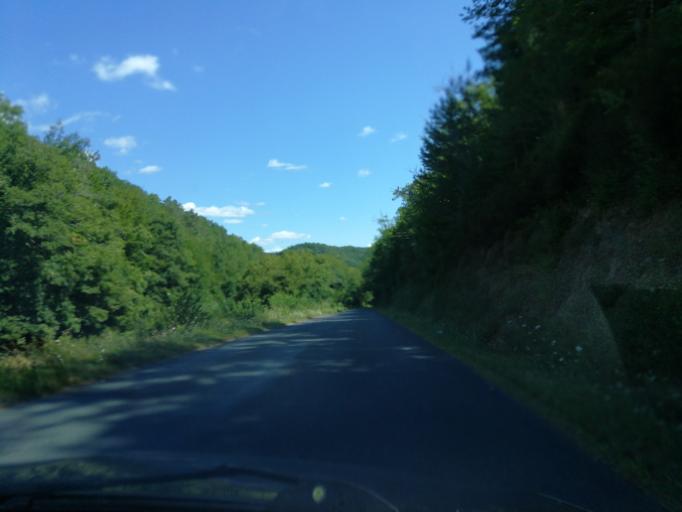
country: FR
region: Limousin
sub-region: Departement de la Correze
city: Argentat
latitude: 45.0913
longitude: 1.9128
